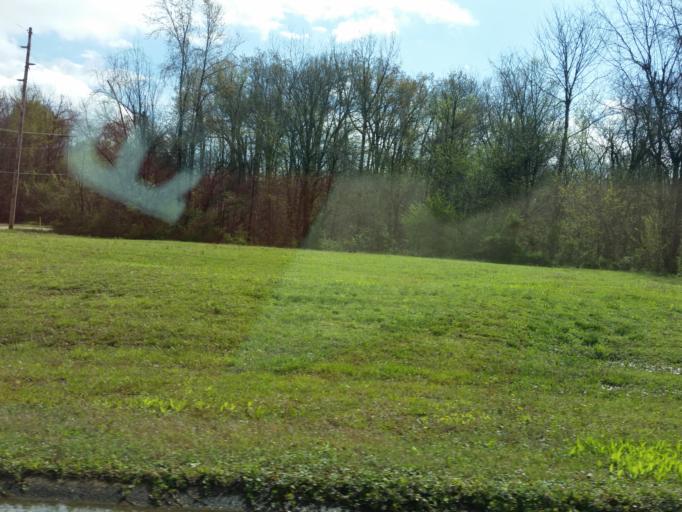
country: US
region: Missouri
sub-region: Butler County
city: Poplar Bluff
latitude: 36.7661
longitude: -90.3936
